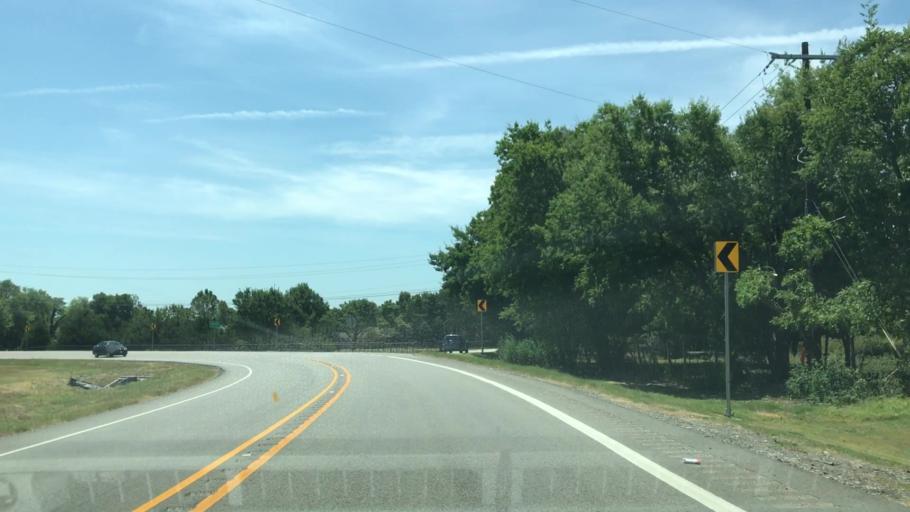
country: US
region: Texas
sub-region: Collin County
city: Fairview
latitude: 33.1207
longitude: -96.6092
